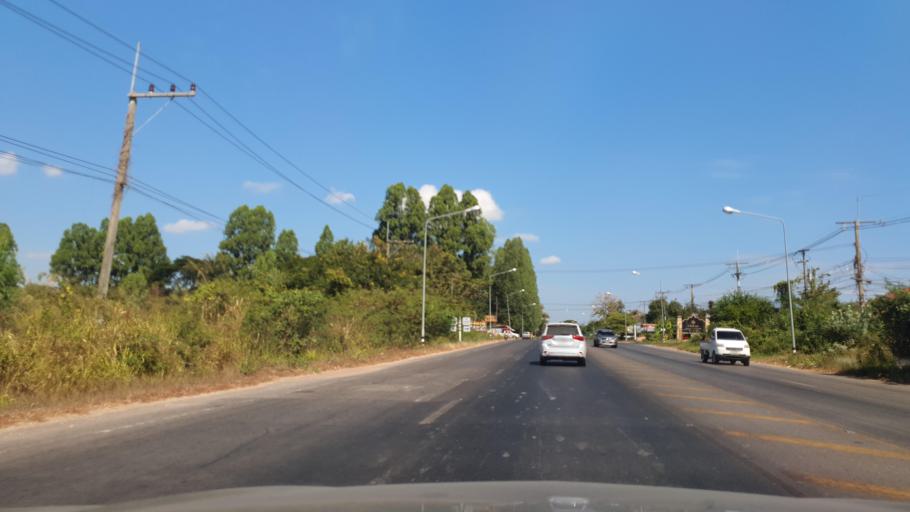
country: TH
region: Kalasin
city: Somdet
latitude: 16.7233
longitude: 103.7596
